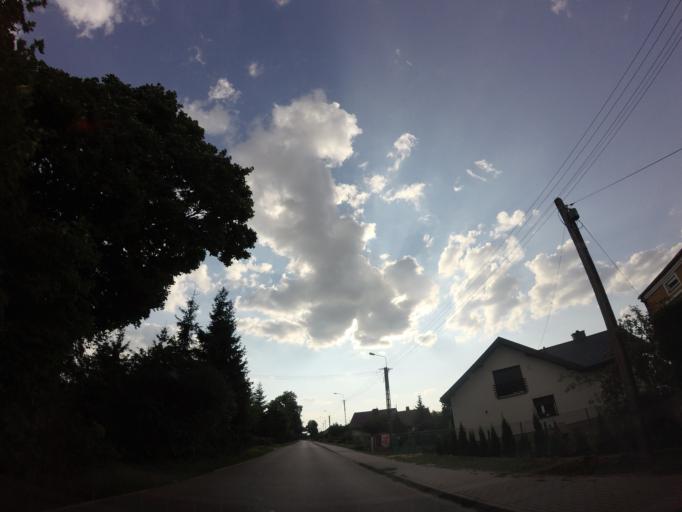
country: PL
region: Lublin Voivodeship
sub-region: Powiat lukowski
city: Wojcieszkow
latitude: 51.7676
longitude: 22.3108
